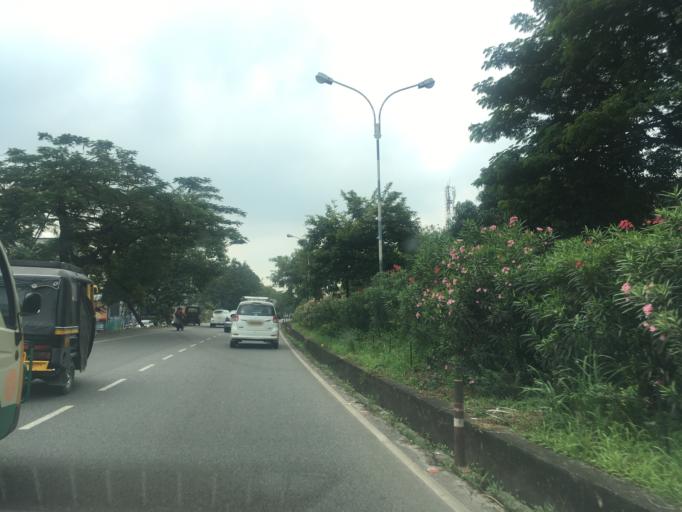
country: IN
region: Kerala
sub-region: Ernakulam
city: Elur
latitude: 10.0206
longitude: 76.3105
